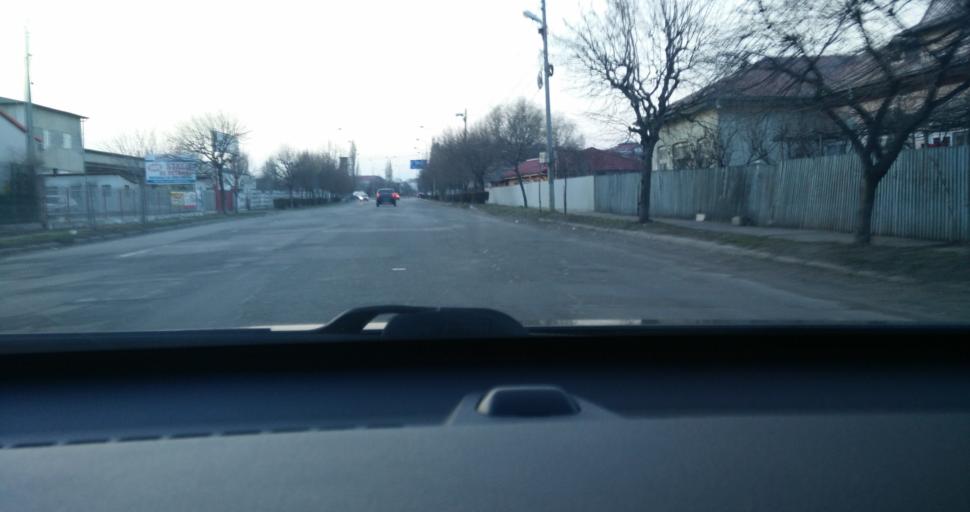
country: RO
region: Vrancea
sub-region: Comuna Vrancioaia
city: Focsani
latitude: 45.6861
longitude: 27.2007
